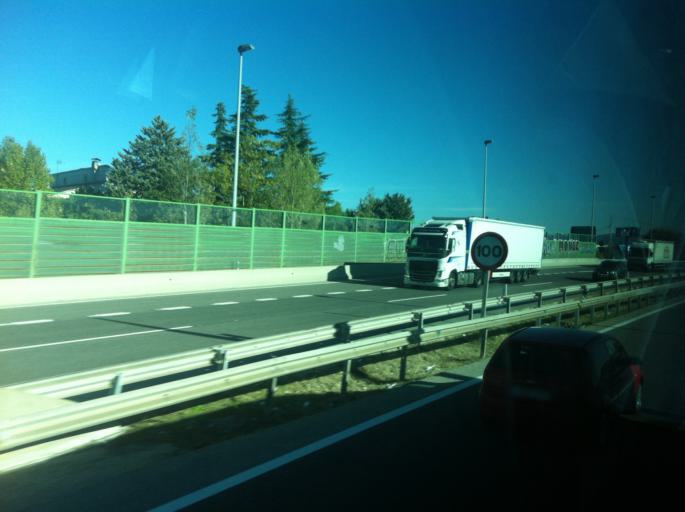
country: ES
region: Madrid
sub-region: Provincia de Madrid
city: La Cabrera
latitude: 40.9226
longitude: -3.6150
